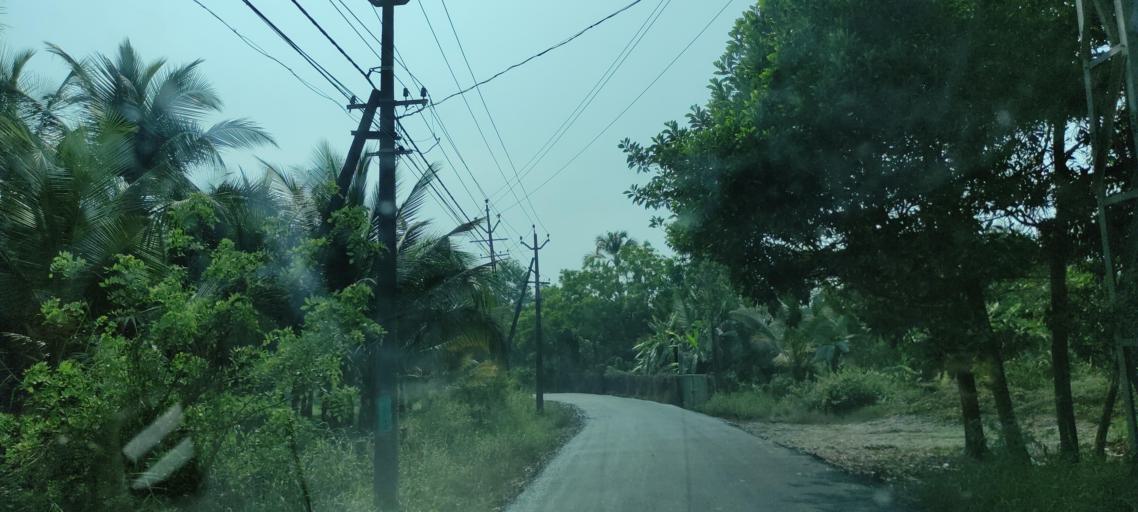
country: IN
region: Kerala
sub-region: Pattanamtitta
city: Tiruvalla
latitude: 9.3606
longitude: 76.4969
